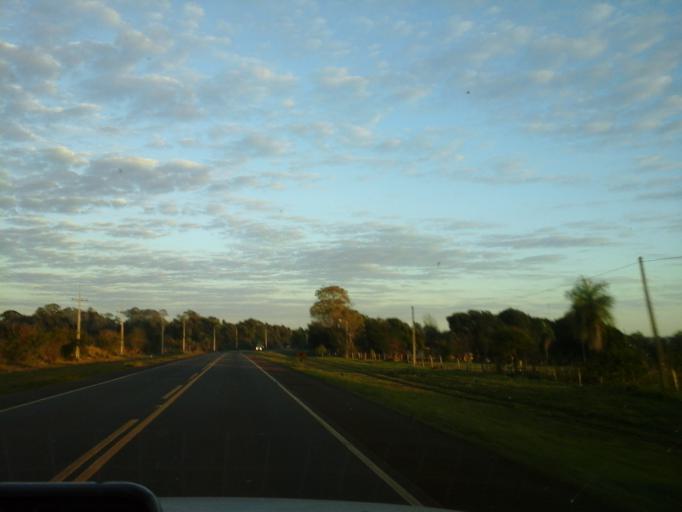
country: PY
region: Misiones
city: San Patricio
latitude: -27.0241
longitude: -56.7076
